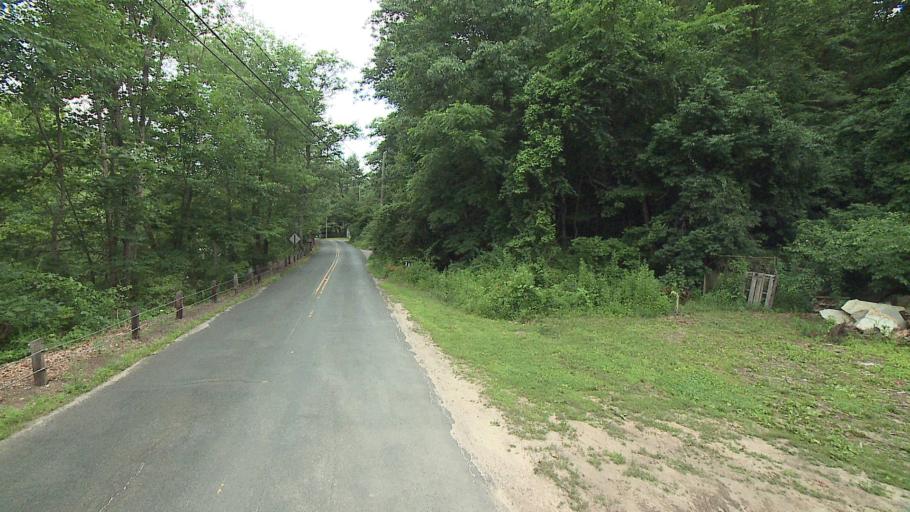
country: US
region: Connecticut
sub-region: Litchfield County
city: New Hartford Center
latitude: 41.9184
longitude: -72.9892
